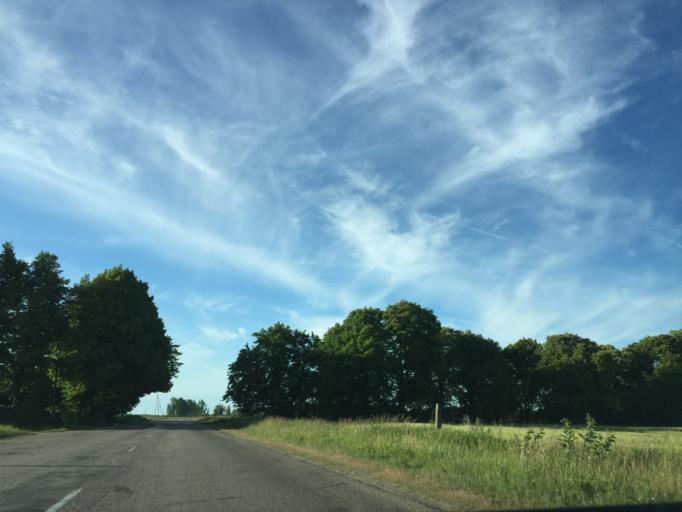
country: LV
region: Ventspils
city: Ventspils
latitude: 57.3306
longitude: 21.5640
